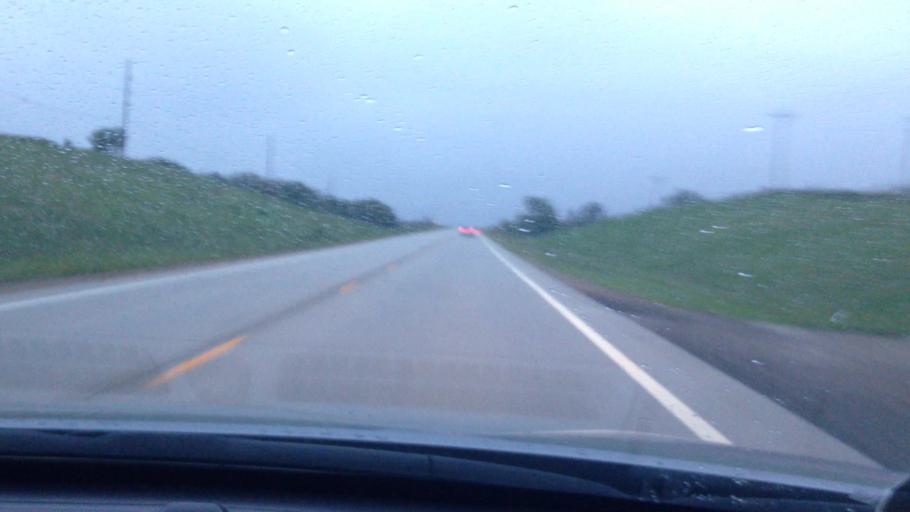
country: US
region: Kansas
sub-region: Brown County
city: Horton
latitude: 39.6675
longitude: -95.4976
